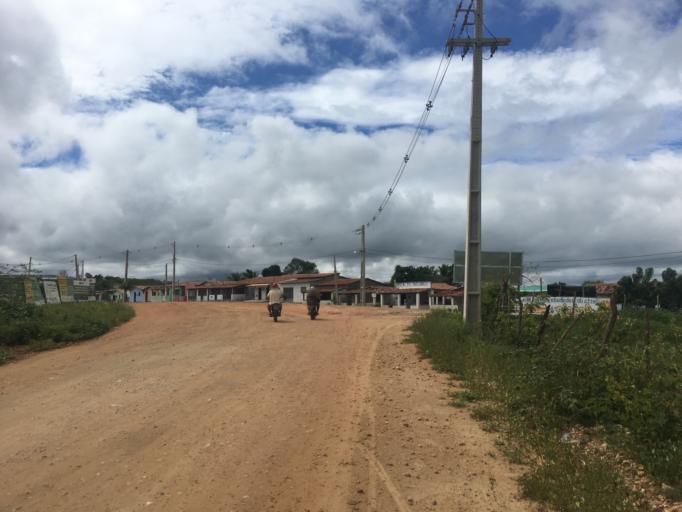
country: BR
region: Rio Grande do Norte
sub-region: Cerro Cora
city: Cerro Cora
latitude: -6.0566
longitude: -36.3610
